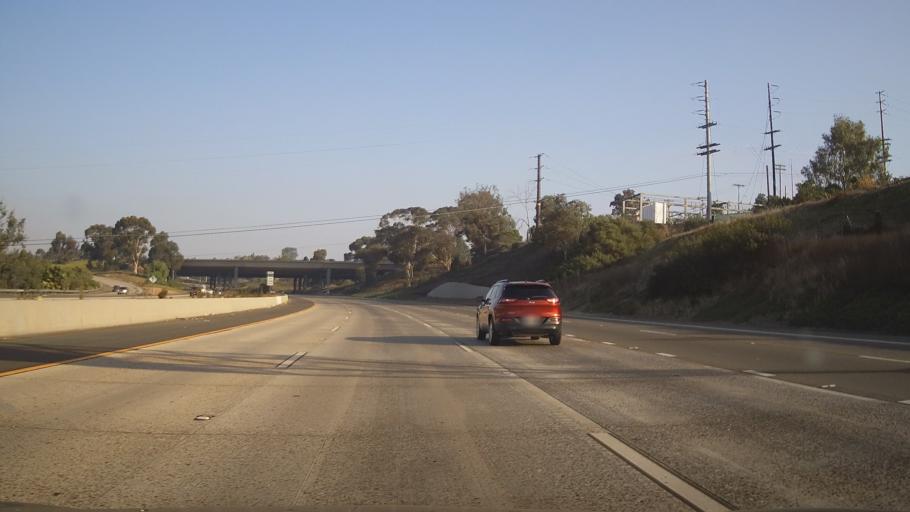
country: US
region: California
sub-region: San Diego County
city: San Diego
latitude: 32.7299
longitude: -117.1112
